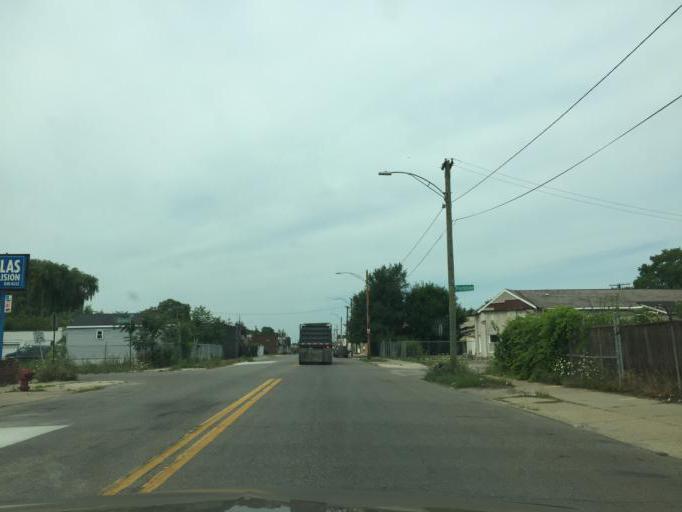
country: US
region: Michigan
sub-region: Wayne County
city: Redford
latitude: 42.4003
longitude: -83.2576
